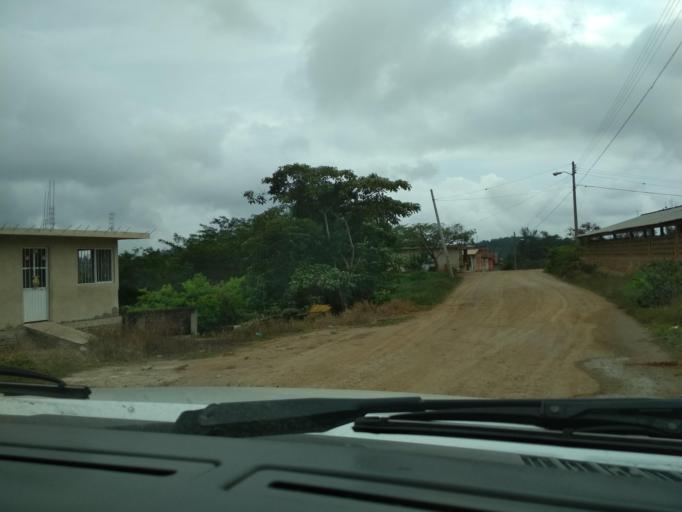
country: MX
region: Veracruz
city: El Castillo
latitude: 19.5438
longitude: -96.8482
